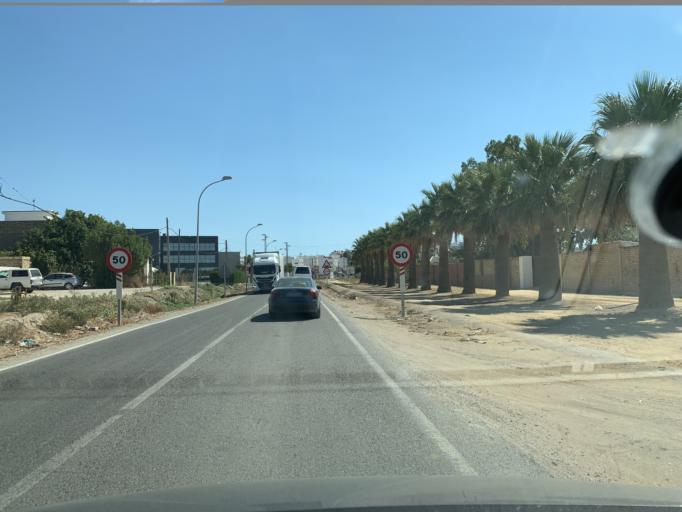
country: ES
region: Andalusia
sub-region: Provincia de Sevilla
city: Marchena
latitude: 37.3361
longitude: -5.4246
